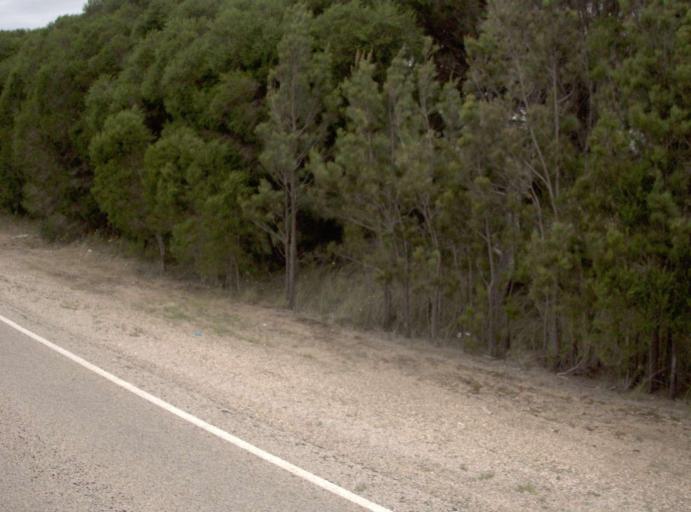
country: AU
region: Victoria
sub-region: East Gippsland
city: Bairnsdale
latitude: -37.8855
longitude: 147.5578
